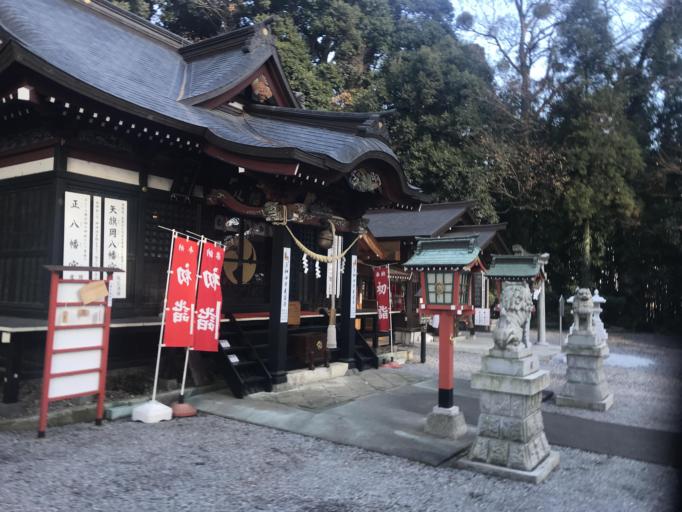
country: JP
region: Tochigi
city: Kaminokawa
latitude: 36.4009
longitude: 139.8781
